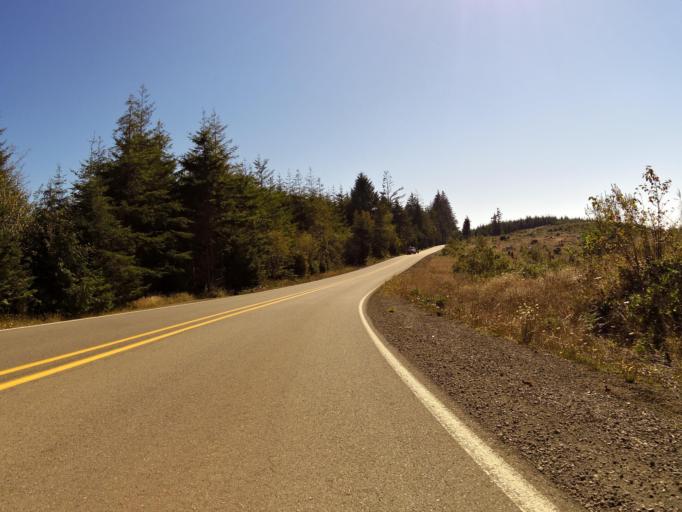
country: US
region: Oregon
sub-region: Coos County
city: Barview
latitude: 43.2555
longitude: -124.3369
